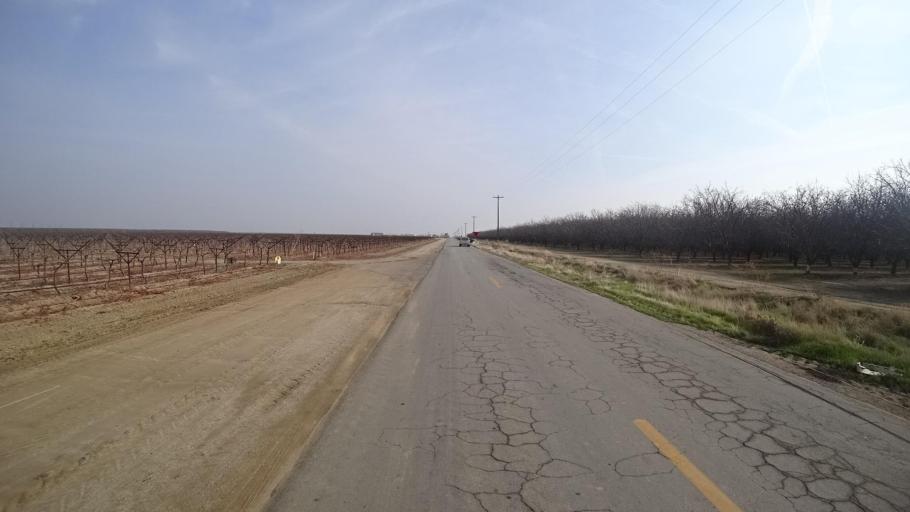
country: US
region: California
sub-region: Kern County
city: Lebec
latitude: 35.0309
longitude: -118.9312
